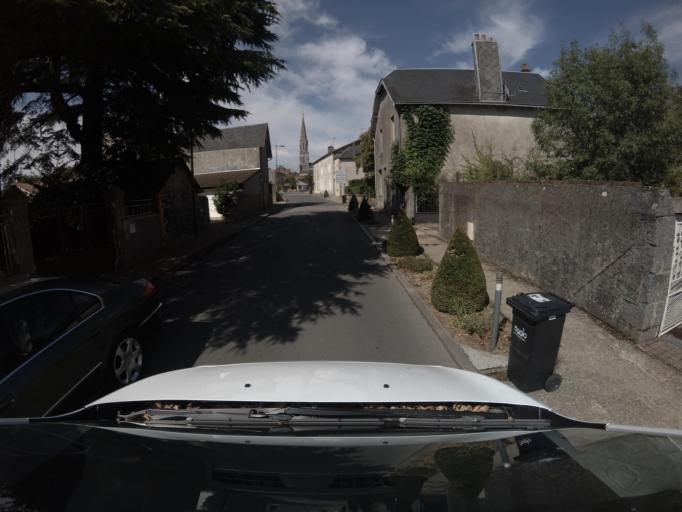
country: FR
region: Poitou-Charentes
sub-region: Departement des Deux-Sevres
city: Nueil-les-Aubiers
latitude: 46.9533
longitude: -0.5904
